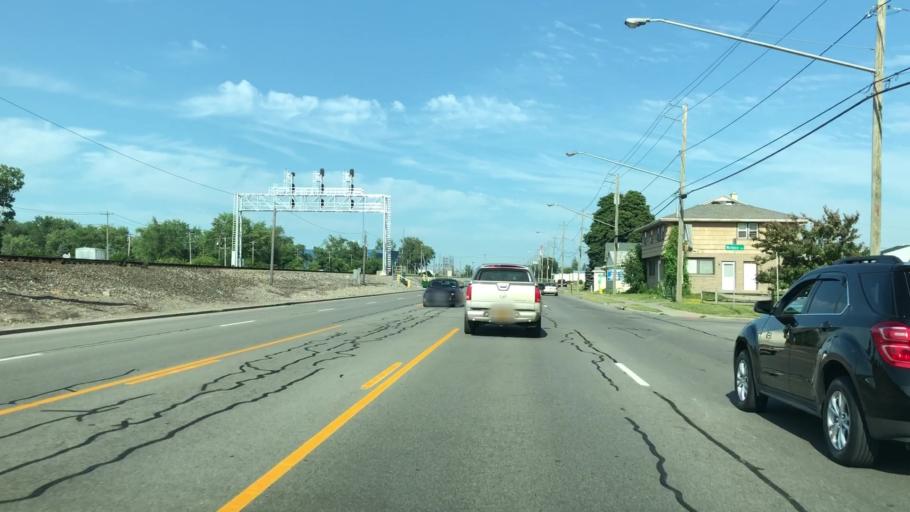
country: US
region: New York
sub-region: Erie County
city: Sloan
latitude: 42.9012
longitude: -78.7784
